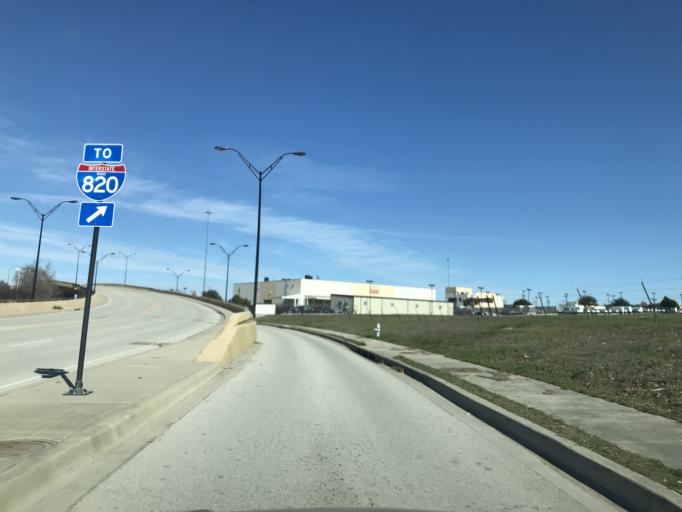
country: US
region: Texas
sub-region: Tarrant County
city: Blue Mound
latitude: 32.8369
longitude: -97.3009
